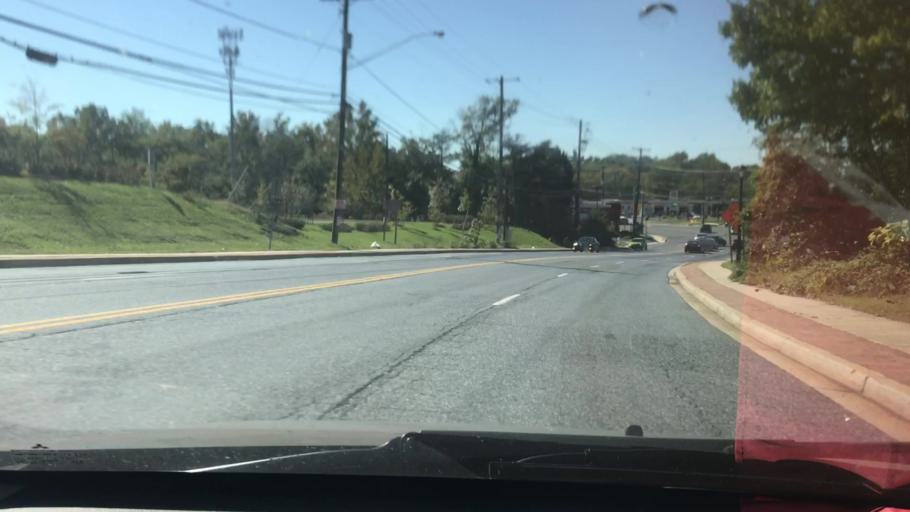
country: US
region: Maryland
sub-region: Prince George's County
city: Peppermill Village
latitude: 38.9101
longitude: -76.8903
